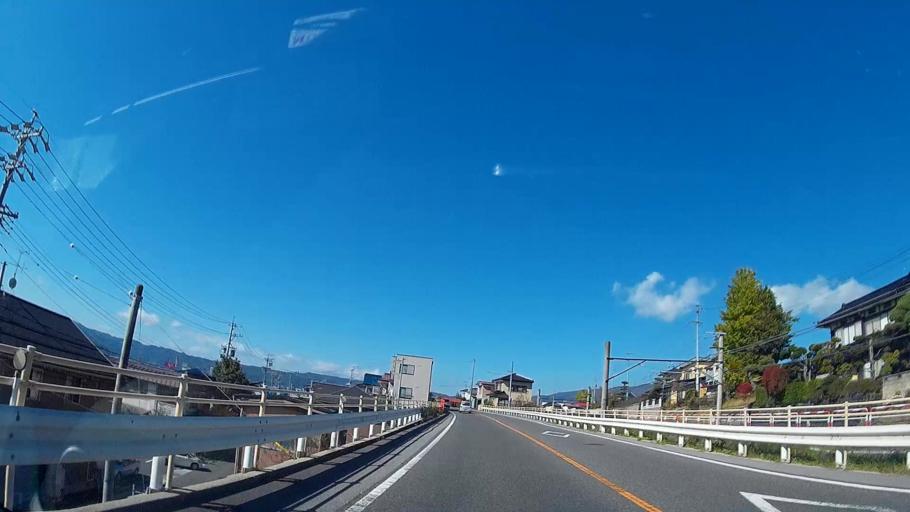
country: JP
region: Nagano
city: Suwa
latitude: 36.0689
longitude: 138.0970
